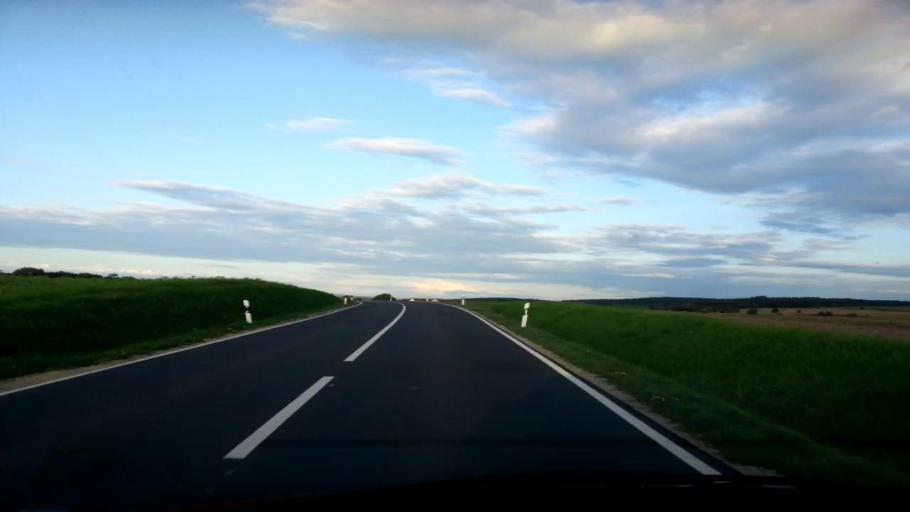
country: DE
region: Bavaria
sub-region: Upper Franconia
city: Burgebrach
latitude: 49.8196
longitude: 10.6866
